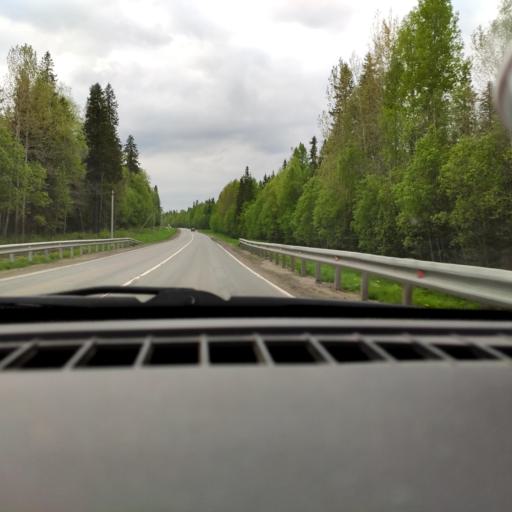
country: RU
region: Perm
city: Perm
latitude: 58.2030
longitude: 56.2023
